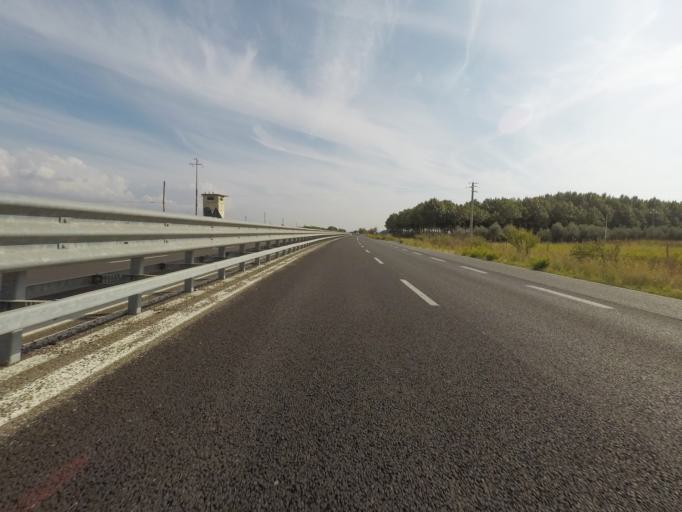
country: IT
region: Latium
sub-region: Provincia di Viterbo
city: Montalto di Castro
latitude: 42.3288
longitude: 11.6312
